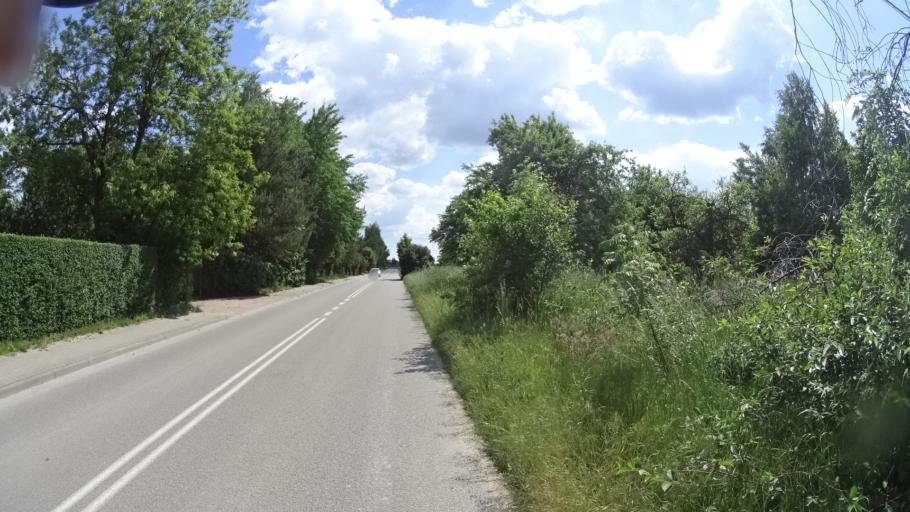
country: PL
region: Masovian Voivodeship
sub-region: Powiat pruszkowski
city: Nadarzyn
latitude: 52.0452
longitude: 20.8265
